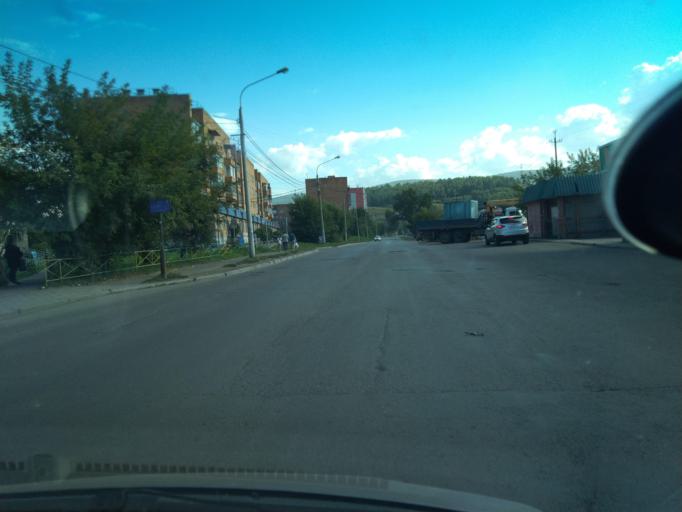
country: RU
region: Krasnoyarskiy
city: Krasnoyarsk
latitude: 55.9734
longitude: 92.9365
